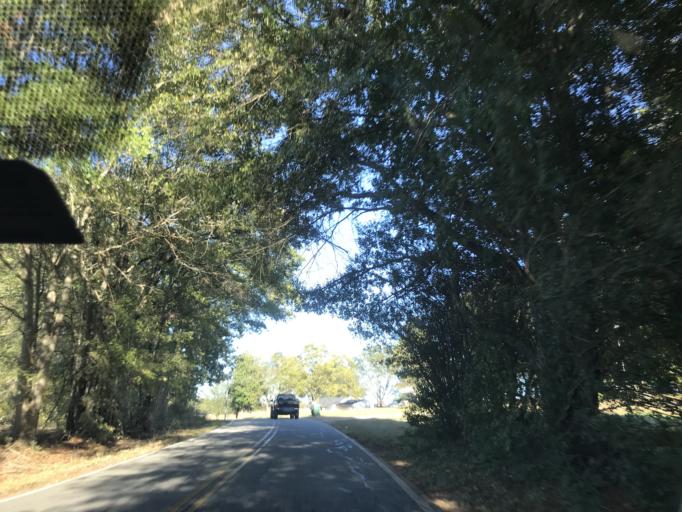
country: US
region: South Carolina
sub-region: Spartanburg County
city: Mayo
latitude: 35.1066
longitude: -81.8356
